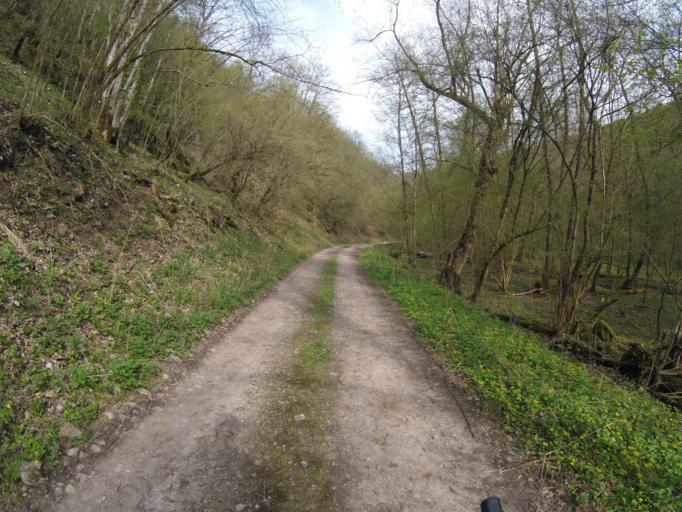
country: HU
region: Borsod-Abauj-Zemplen
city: Rudabanya
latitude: 48.5329
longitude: 20.6522
